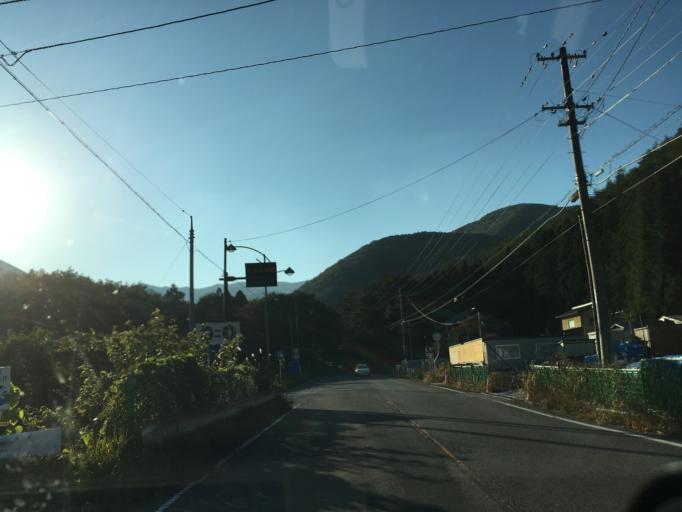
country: JP
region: Fukushima
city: Koriyama
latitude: 37.3918
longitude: 140.2248
